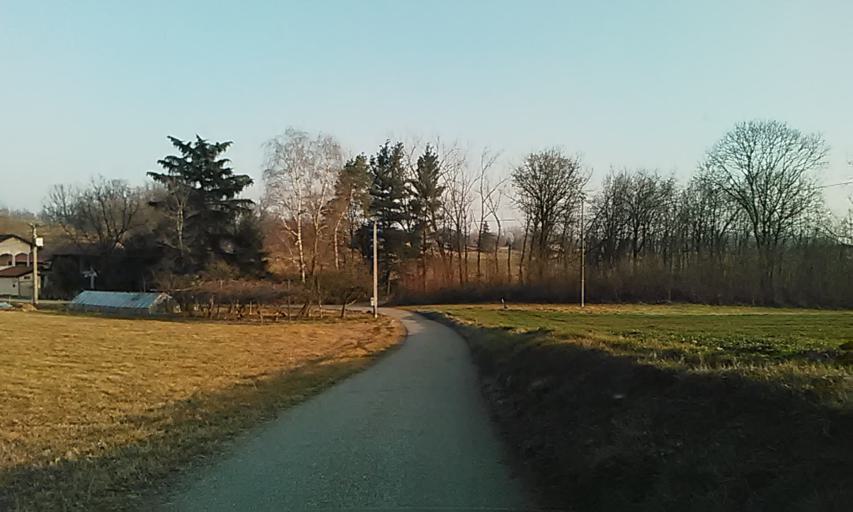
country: IT
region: Piedmont
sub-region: Provincia di Biella
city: Dorzano
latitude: 45.4147
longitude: 8.1163
